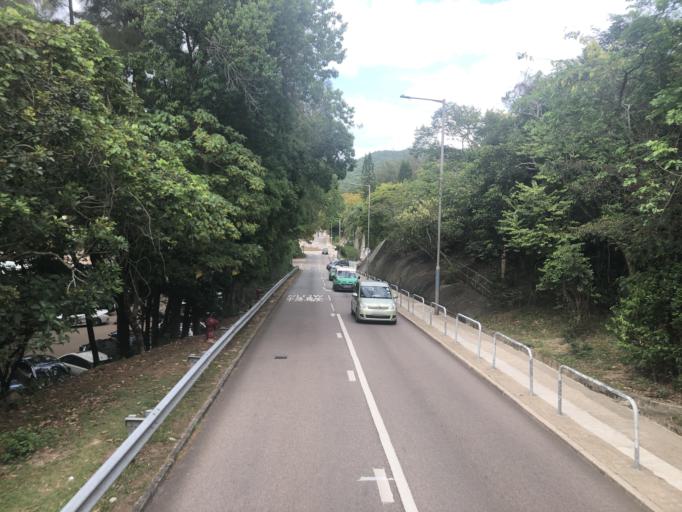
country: HK
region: Sai Kung
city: Sai Kung
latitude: 22.3960
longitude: 114.3183
